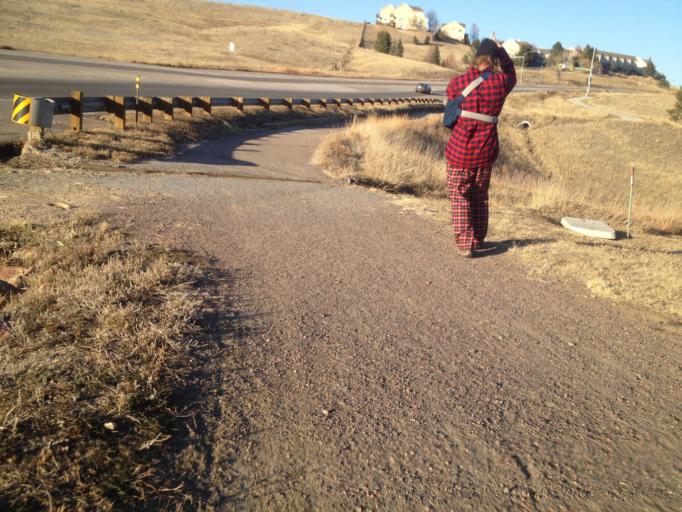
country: US
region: Colorado
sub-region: Boulder County
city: Superior
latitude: 39.9357
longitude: -105.1656
